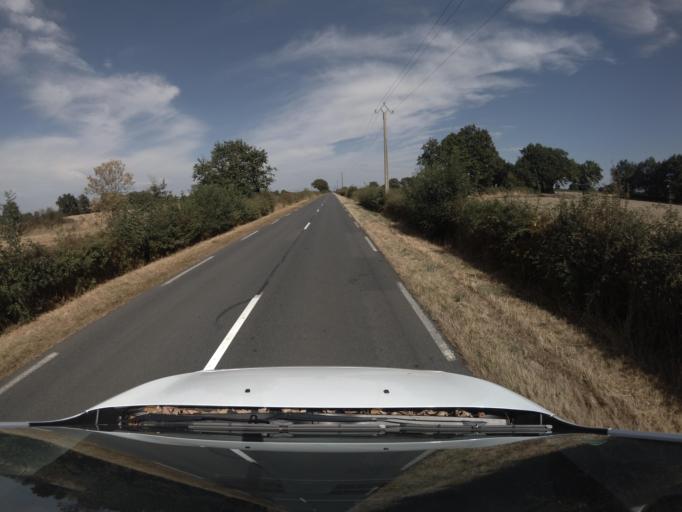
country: FR
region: Poitou-Charentes
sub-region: Departement des Deux-Sevres
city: Argenton-les-Vallees
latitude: 46.9799
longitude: -0.5063
